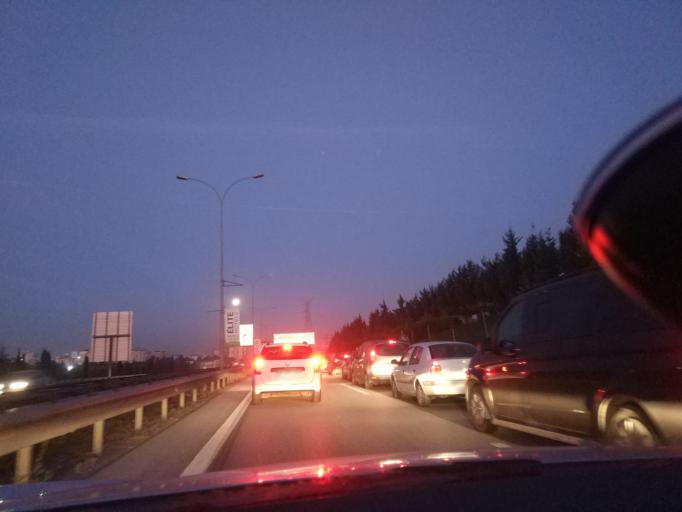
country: TR
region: Istanbul
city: Pendik
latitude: 40.9145
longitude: 29.3182
